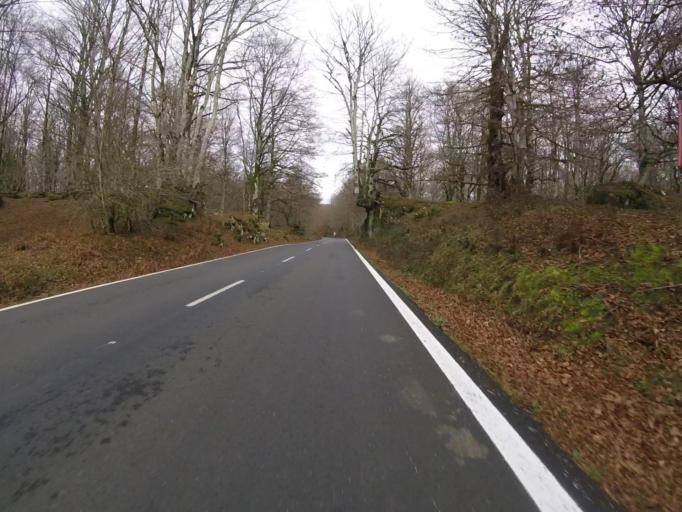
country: ES
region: Navarre
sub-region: Provincia de Navarra
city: Olazagutia
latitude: 42.8429
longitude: -2.1801
